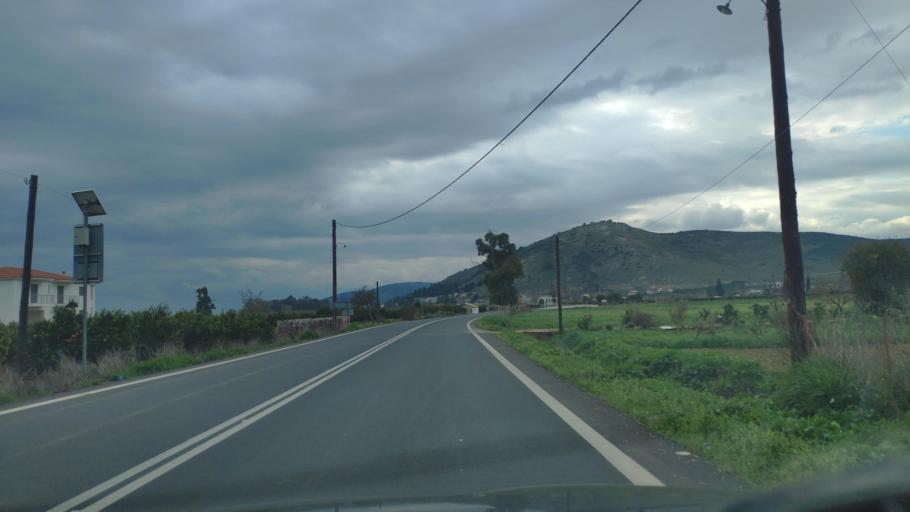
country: GR
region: Peloponnese
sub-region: Nomos Argolidos
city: Nea Kios
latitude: 37.5682
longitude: 22.7104
